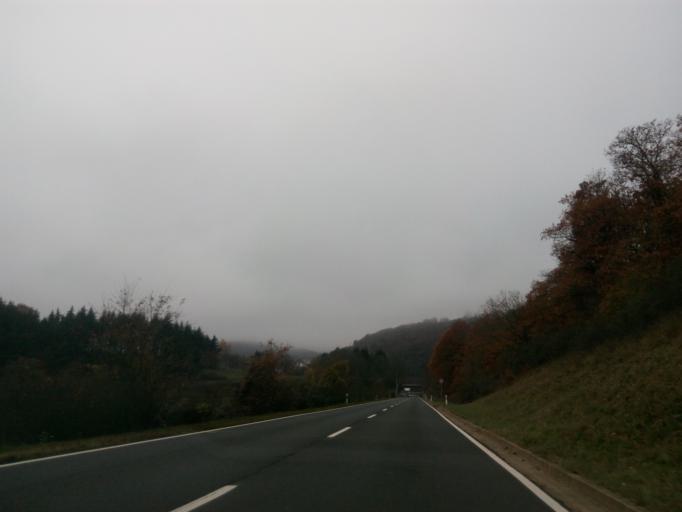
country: DE
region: Rheinland-Pfalz
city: Fischbach
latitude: 49.7427
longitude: 7.4174
